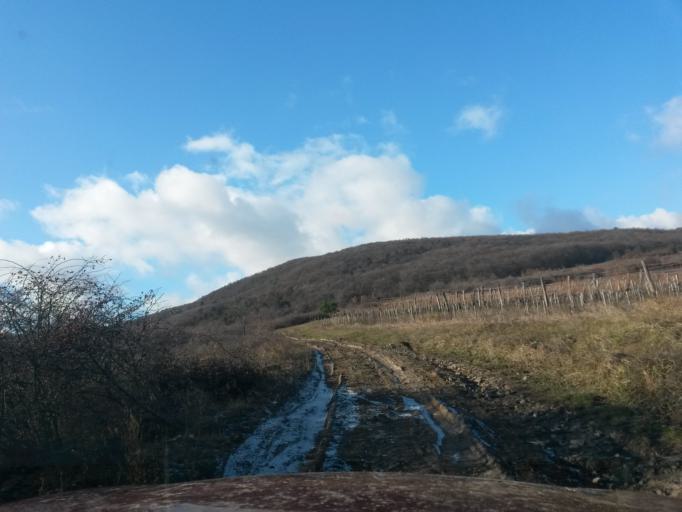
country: HU
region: Borsod-Abauj-Zemplen
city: Sarospatak
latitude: 48.3332
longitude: 21.5185
